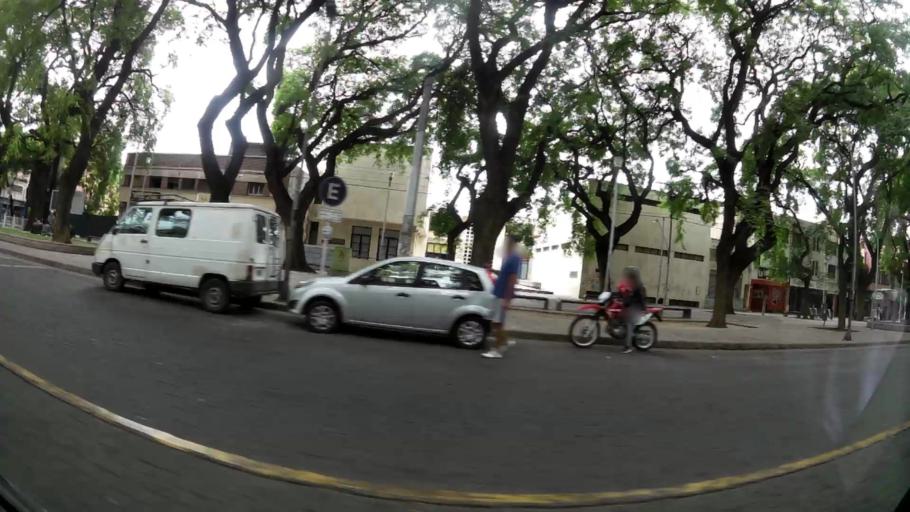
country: AR
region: Mendoza
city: Mendoza
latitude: -32.8815
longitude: -68.8370
